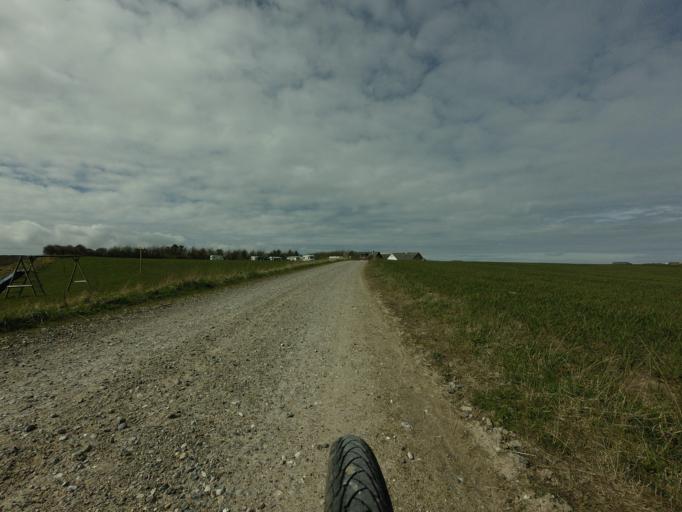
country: DK
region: North Denmark
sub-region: Jammerbugt Kommune
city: Pandrup
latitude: 57.3848
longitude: 9.7398
